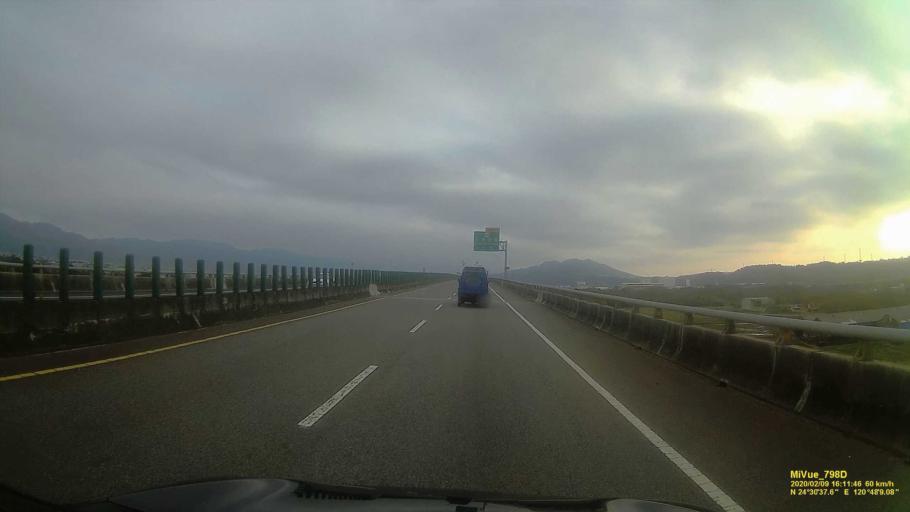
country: TW
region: Taiwan
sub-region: Miaoli
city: Miaoli
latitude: 24.5100
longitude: 120.8026
